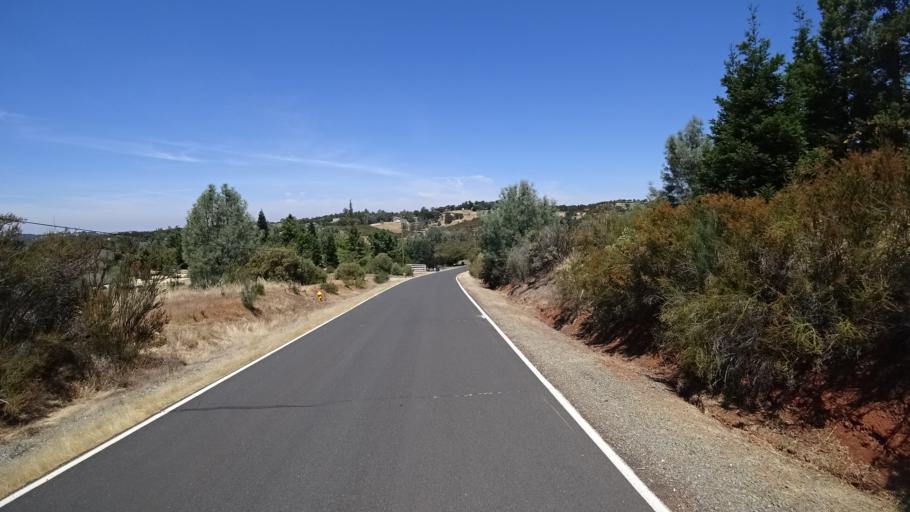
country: US
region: California
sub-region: Calaveras County
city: Rancho Calaveras
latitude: 38.1241
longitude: -120.8512
